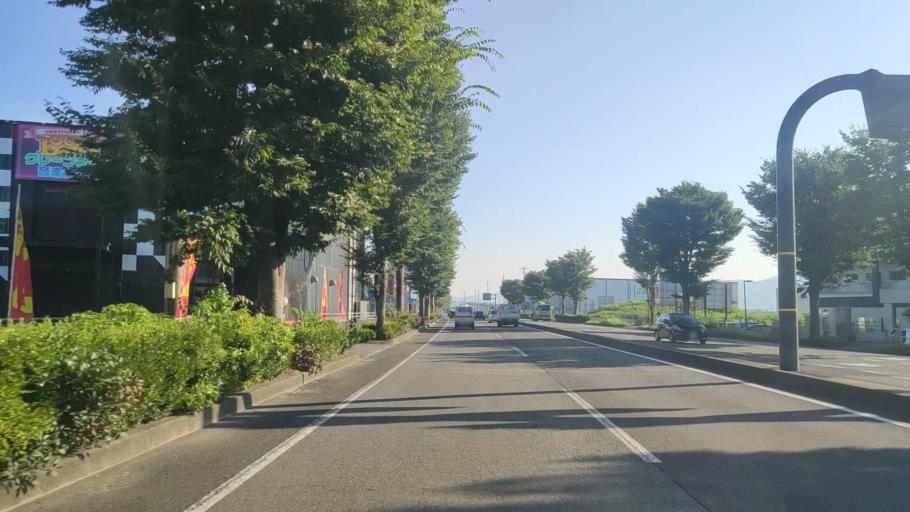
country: JP
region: Fukui
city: Fukui-shi
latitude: 36.0987
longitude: 136.2529
